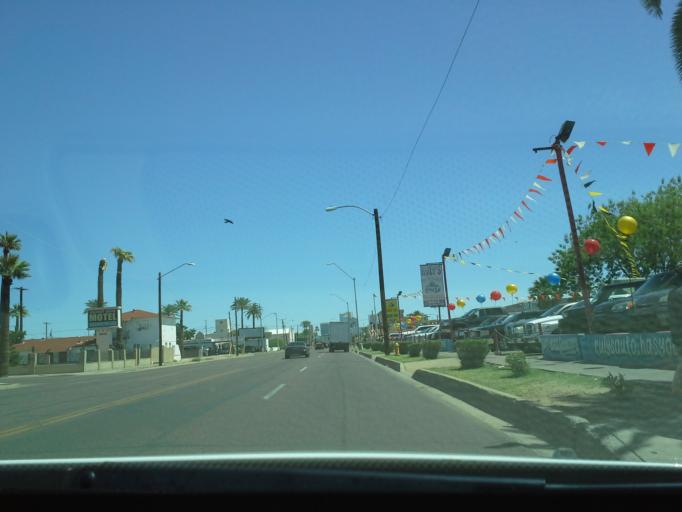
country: US
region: Arizona
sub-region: Maricopa County
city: Phoenix
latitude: 33.4512
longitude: -112.1039
